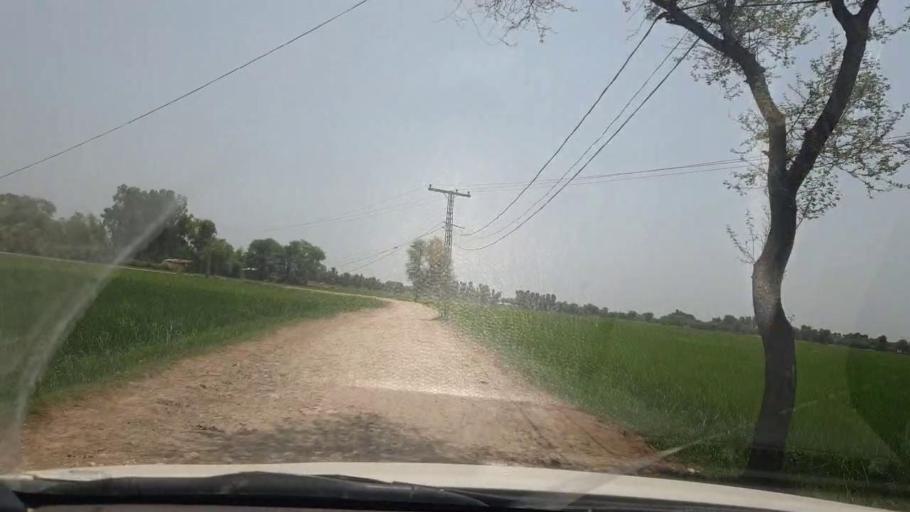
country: PK
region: Sindh
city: Shikarpur
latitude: 27.9193
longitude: 68.6915
